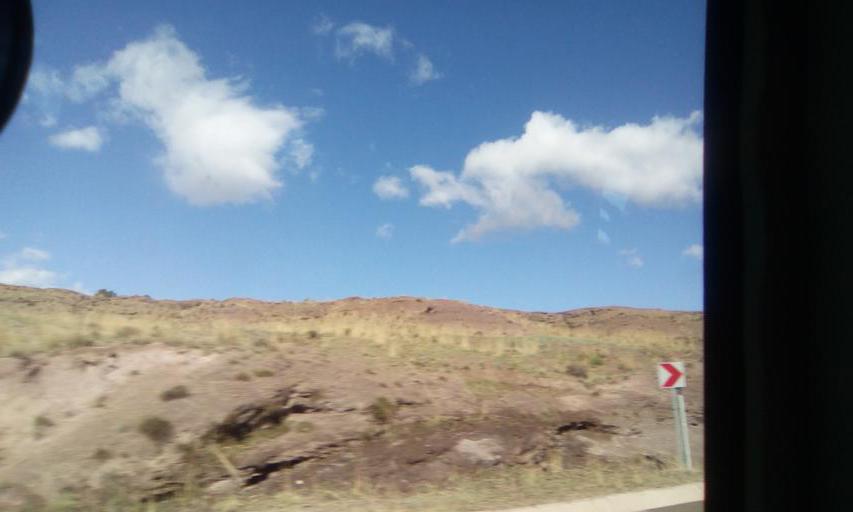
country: LS
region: Qacha's Nek
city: Qacha's Nek
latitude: -30.0421
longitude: 28.2659
